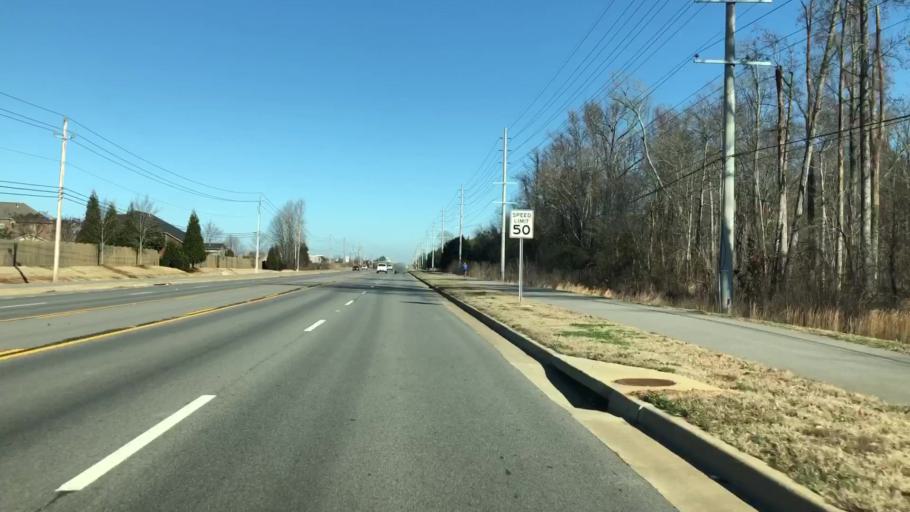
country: US
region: Alabama
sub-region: Madison County
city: Madison
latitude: 34.7236
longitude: -86.7863
